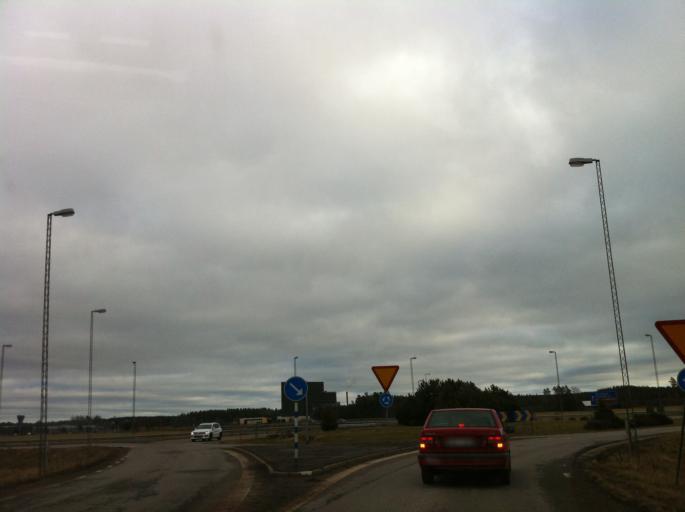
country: SE
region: Kalmar
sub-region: Vimmerby Kommun
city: Vimmerby
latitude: 57.6498
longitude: 15.8128
